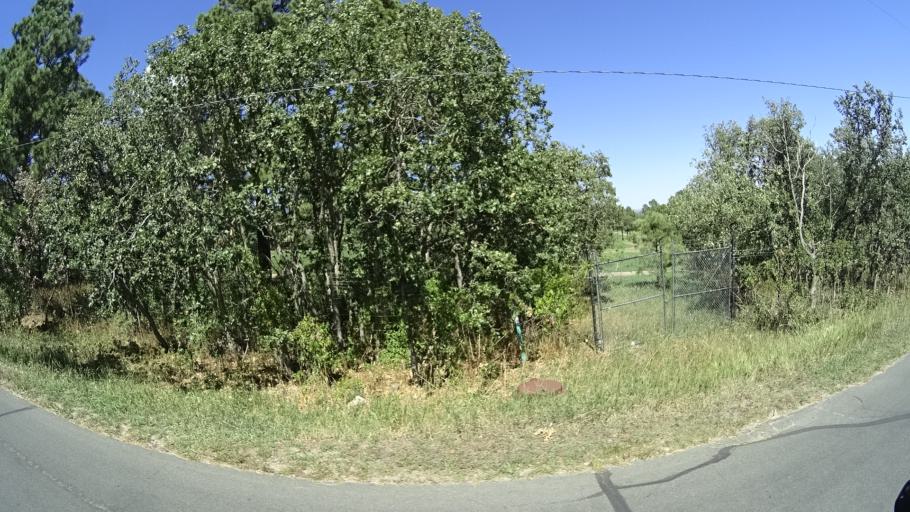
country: US
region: Colorado
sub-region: El Paso County
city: Colorado Springs
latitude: 38.7770
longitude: -104.8448
